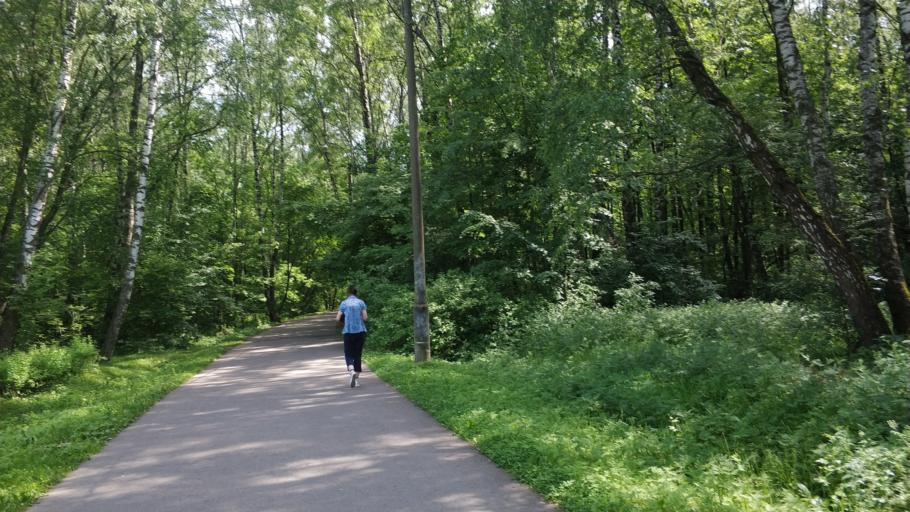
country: RU
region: Moscow
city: Perovo
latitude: 55.7333
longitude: 37.7995
